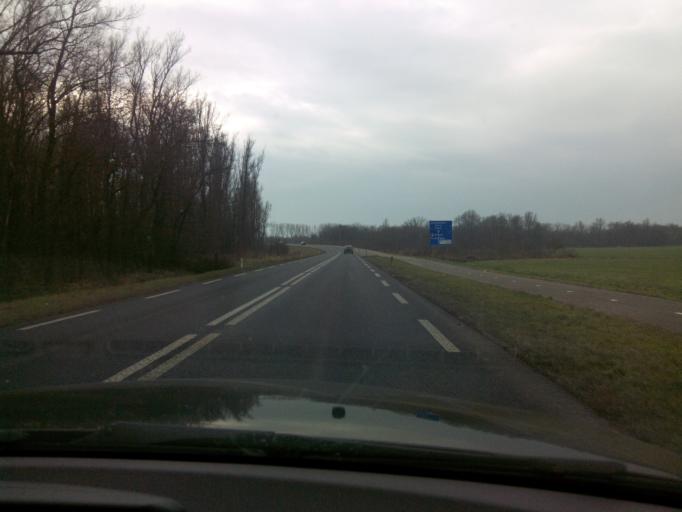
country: NL
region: South Holland
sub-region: Gemeente Leerdam
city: Leerdam
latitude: 51.8713
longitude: 5.0913
